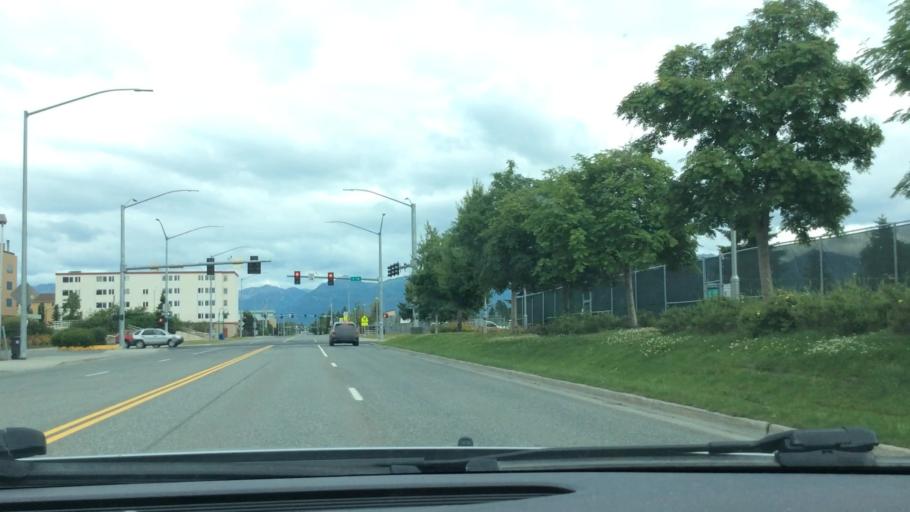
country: US
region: Alaska
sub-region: Anchorage Municipality
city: Anchorage
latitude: 61.2136
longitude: -149.8890
